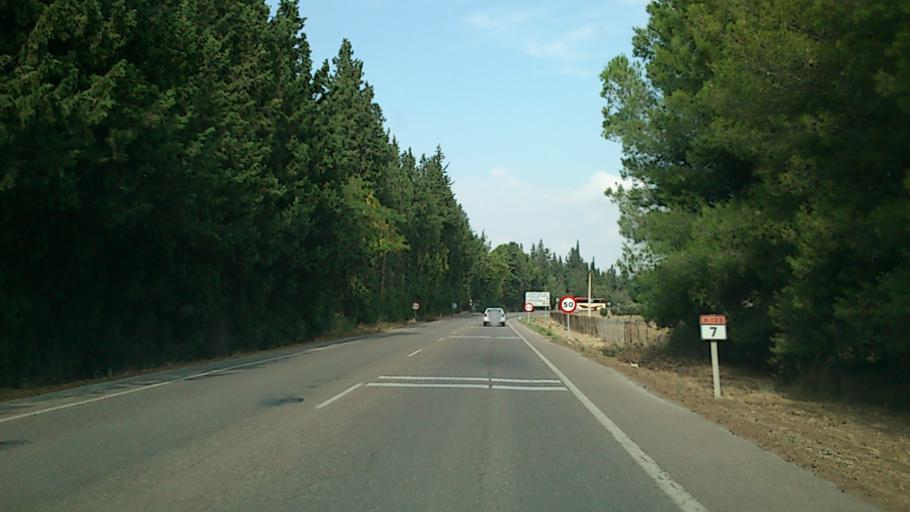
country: ES
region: Aragon
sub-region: Provincia de Zaragoza
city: Villanueva de Gallego
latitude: 41.7218
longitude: -0.8105
